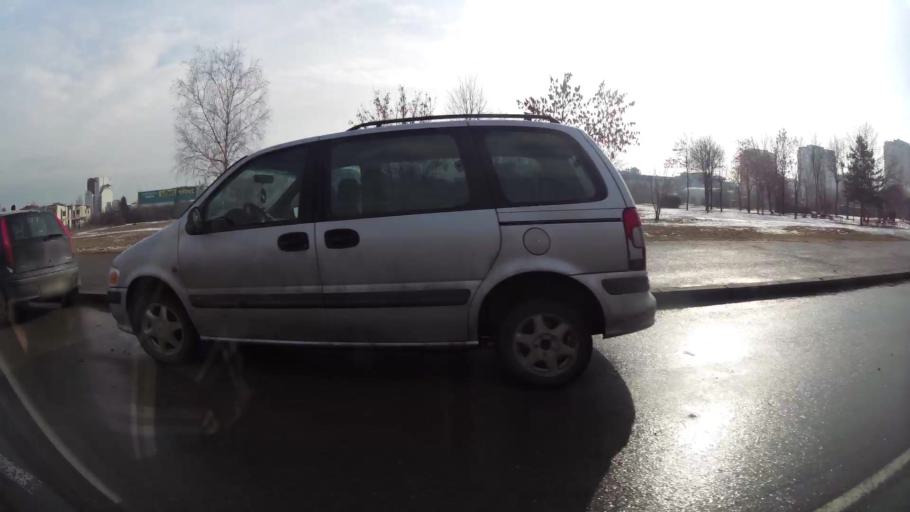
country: BG
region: Sofiya
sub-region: Obshtina Bozhurishte
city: Bozhurishte
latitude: 42.7175
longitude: 23.2528
